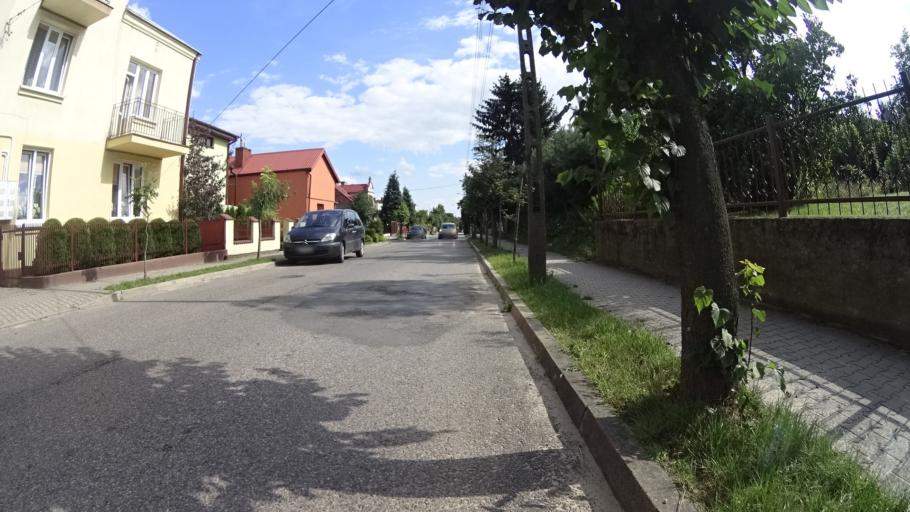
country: PL
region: Masovian Voivodeship
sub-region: Powiat grojecki
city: Mogielnica
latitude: 51.6968
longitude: 20.7179
